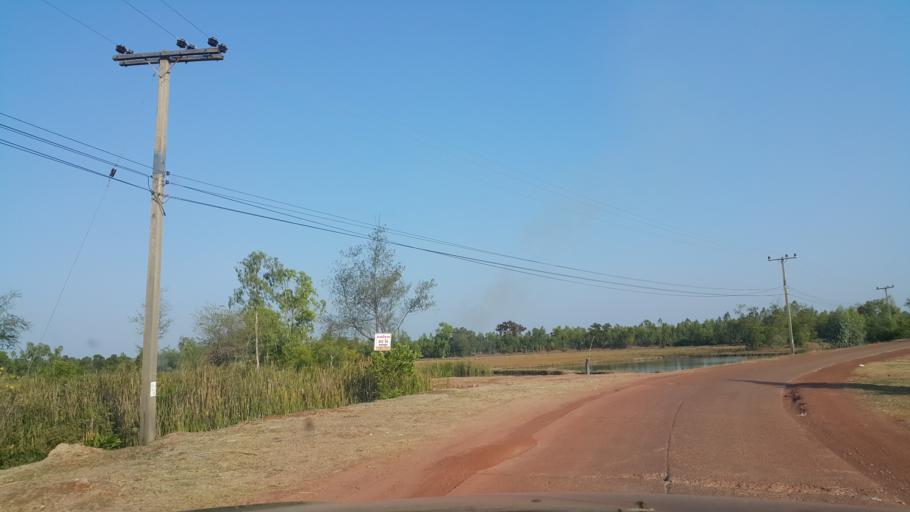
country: TH
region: Changwat Udon Thani
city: Ban Na Muang
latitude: 17.2348
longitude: 103.0708
